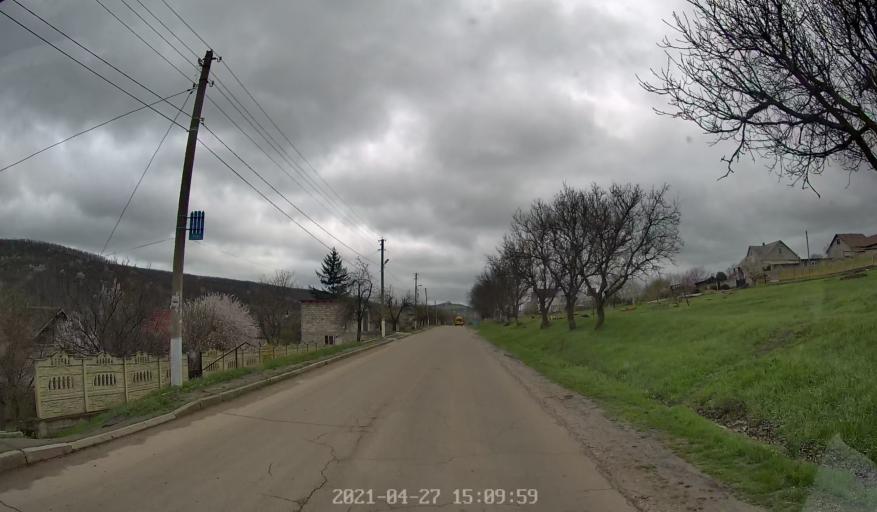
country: MD
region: Chisinau
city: Vadul lui Voda
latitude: 47.0448
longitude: 29.0334
